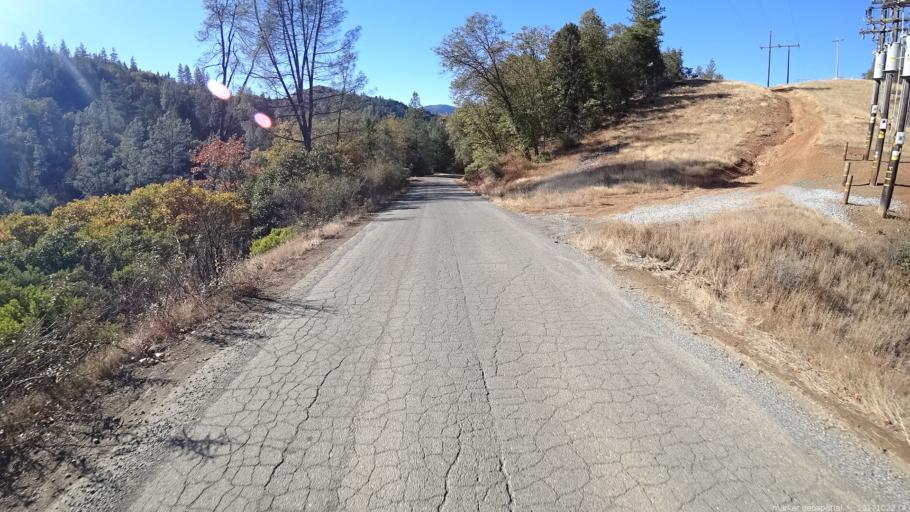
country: US
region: California
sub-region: Shasta County
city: Shasta Lake
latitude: 40.8721
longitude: -122.3593
